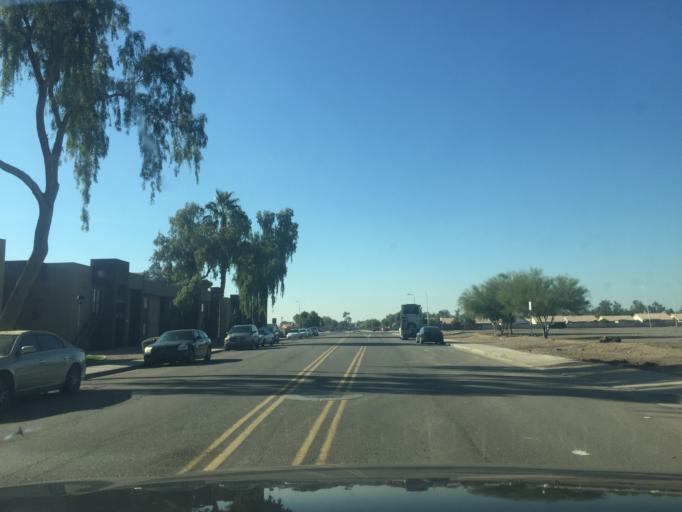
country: US
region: Arizona
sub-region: Maricopa County
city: Tolleson
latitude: 33.4690
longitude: -112.2362
